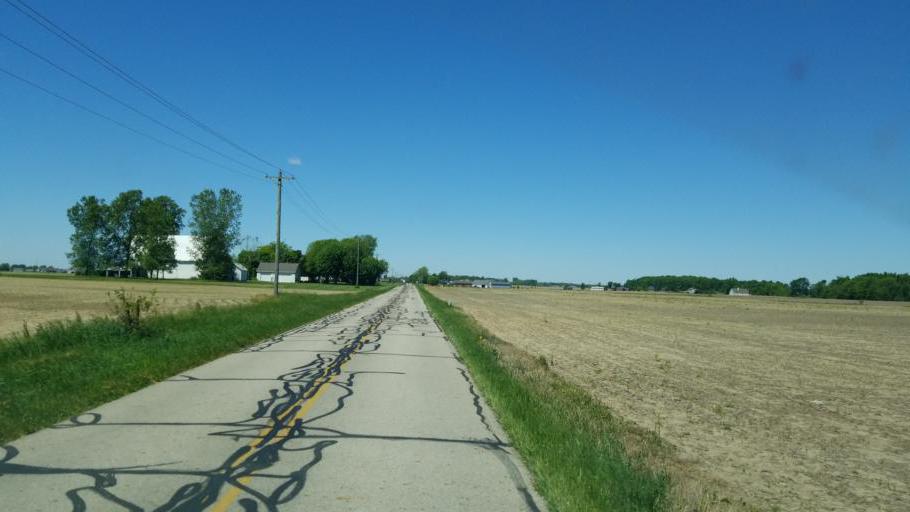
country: US
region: Ohio
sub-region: Shelby County
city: Anna
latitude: 40.3803
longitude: -84.2269
